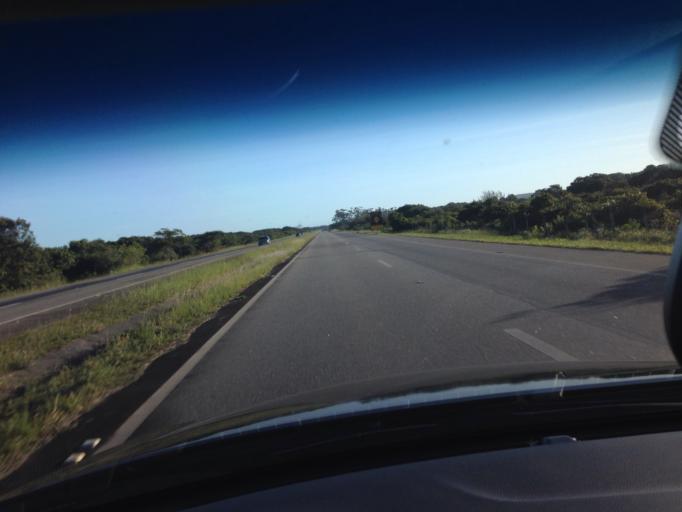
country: BR
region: Espirito Santo
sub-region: Guarapari
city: Guarapari
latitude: -20.5920
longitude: -40.4252
